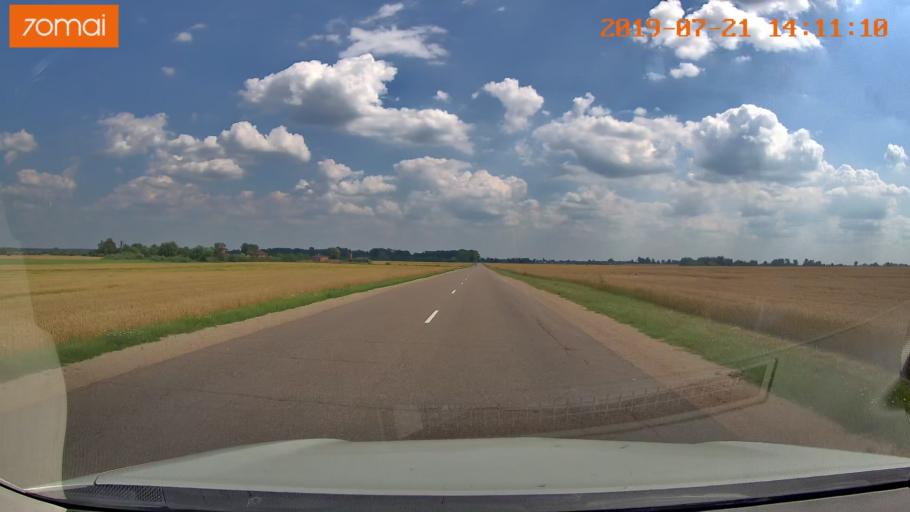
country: BY
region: Grodnenskaya
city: Karelichy
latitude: 53.6595
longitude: 26.1466
